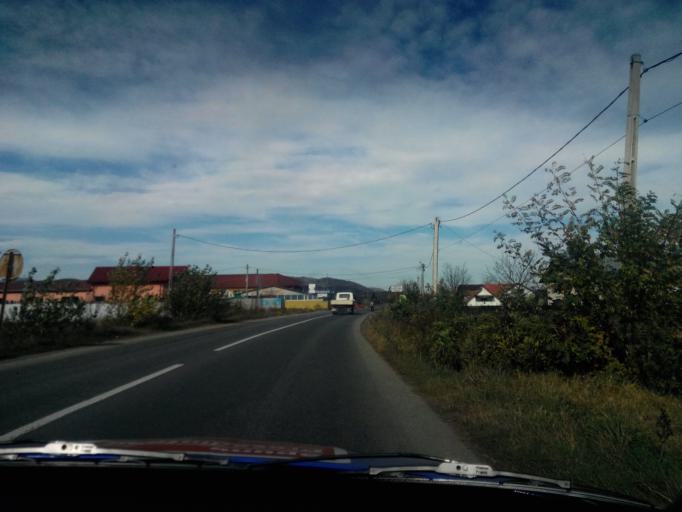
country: RO
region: Bacau
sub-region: Municipiul Onesti
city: Onesti
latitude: 46.2772
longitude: 26.7644
